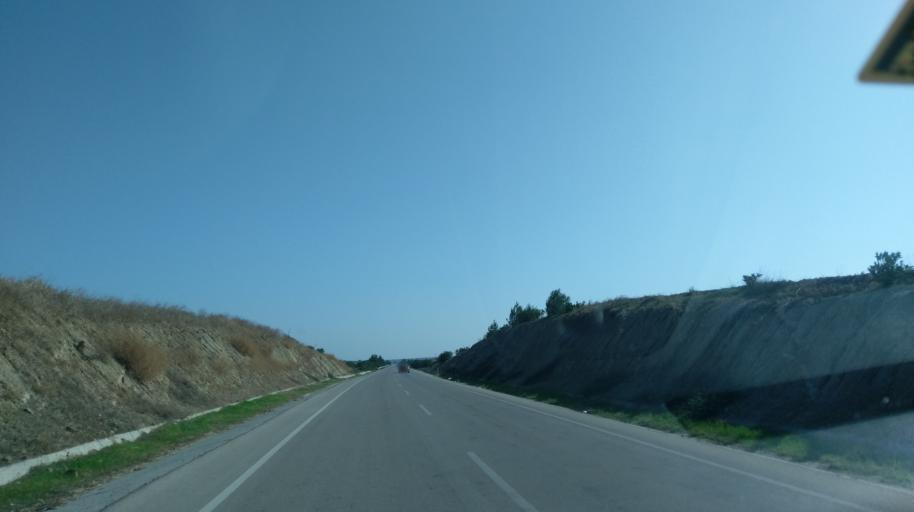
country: CY
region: Ammochostos
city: Leonarisso
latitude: 35.3831
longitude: 34.0174
